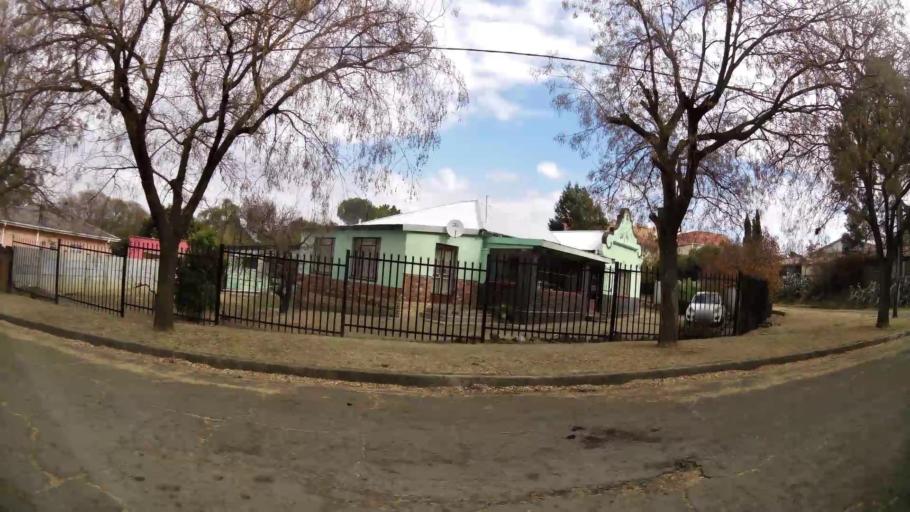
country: ZA
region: Orange Free State
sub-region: Fezile Dabi District Municipality
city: Kroonstad
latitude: -27.6553
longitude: 27.2340
